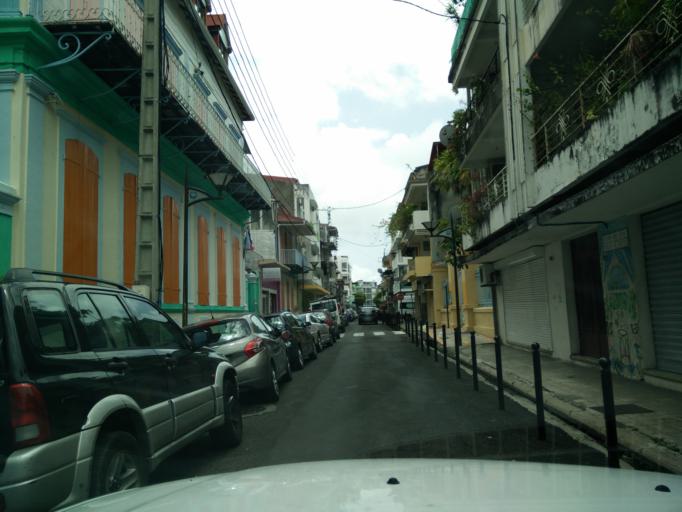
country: GP
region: Guadeloupe
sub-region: Guadeloupe
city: Pointe-a-Pitre
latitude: 16.2378
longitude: -61.5379
